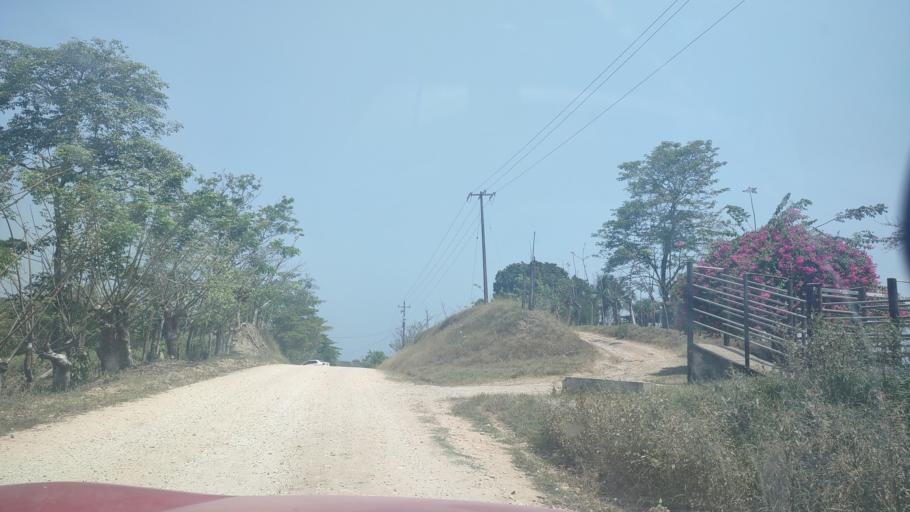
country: MX
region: Tabasco
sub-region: Huimanguillo
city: Francisco Rueda
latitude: 17.6835
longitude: -94.0318
